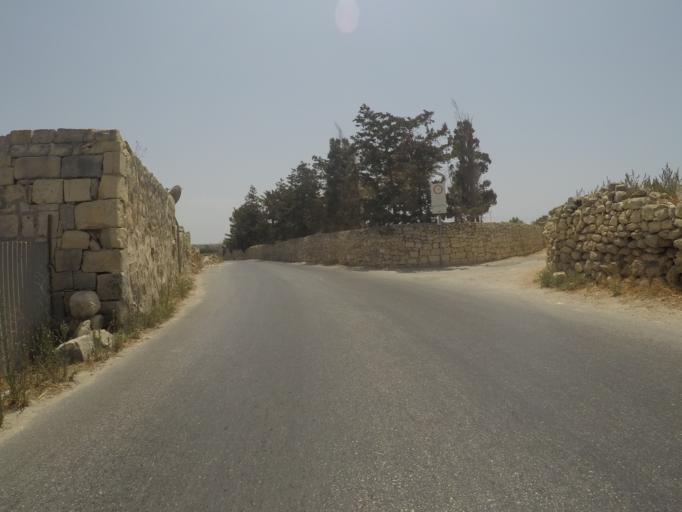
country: MT
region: Is-Siggiewi
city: Siggiewi
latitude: 35.8518
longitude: 14.4312
